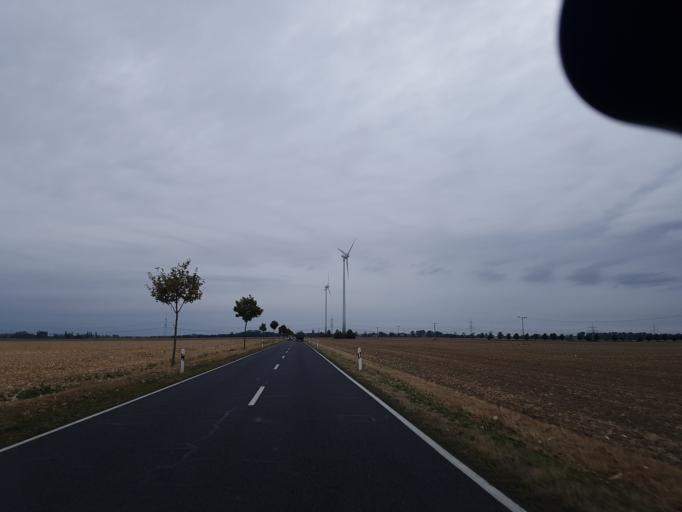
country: DE
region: Saxony-Anhalt
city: Prettin
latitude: 51.6834
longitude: 12.9029
